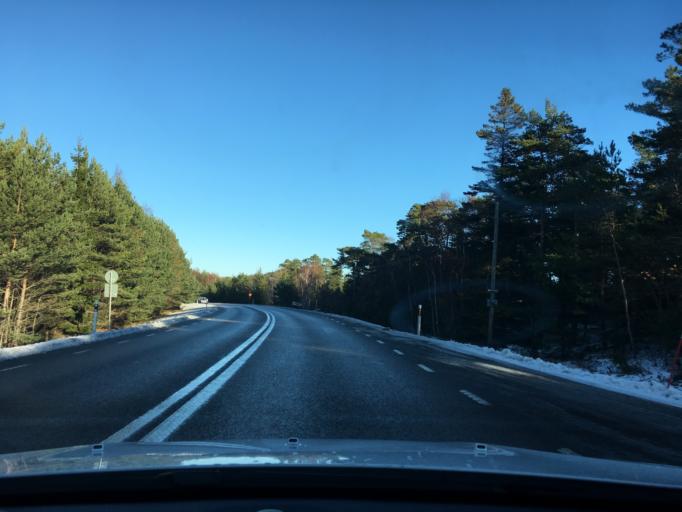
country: SE
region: Vaestra Goetaland
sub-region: Tjorns Kommun
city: Myggenas
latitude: 58.0951
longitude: 11.7071
